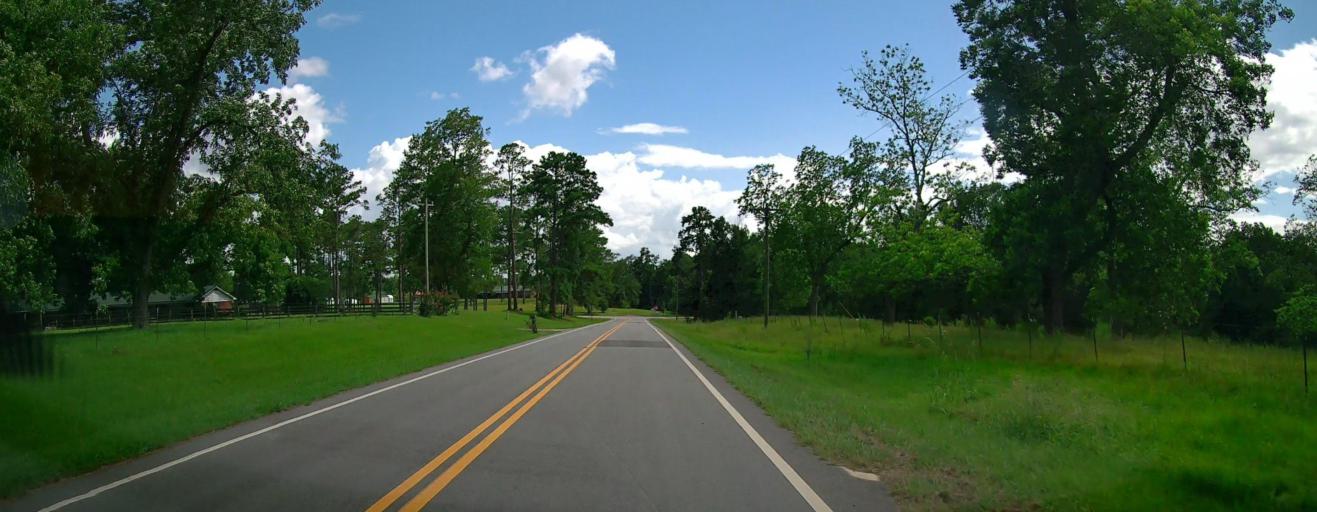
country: US
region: Georgia
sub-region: Irwin County
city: Ocilla
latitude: 31.5977
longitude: -83.1653
